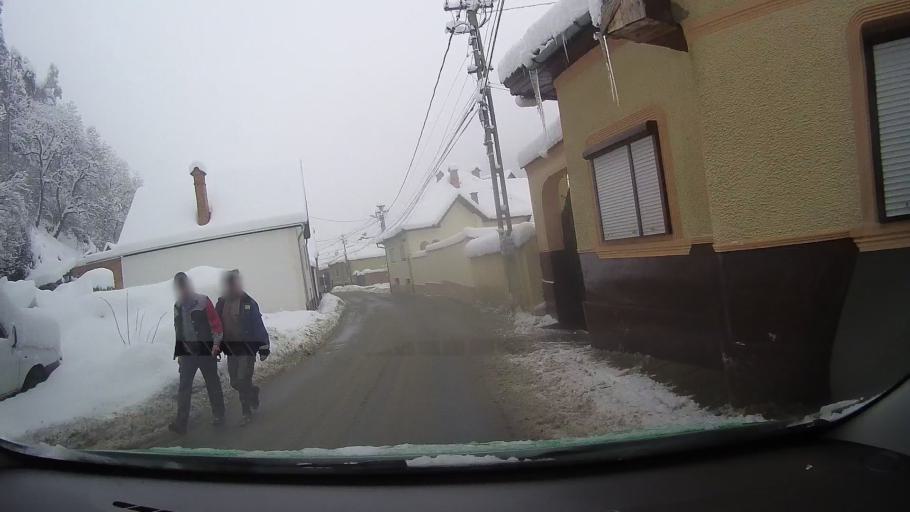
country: RO
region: Sibiu
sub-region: Comuna Tilisca
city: Tilisca
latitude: 45.8016
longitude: 23.8365
